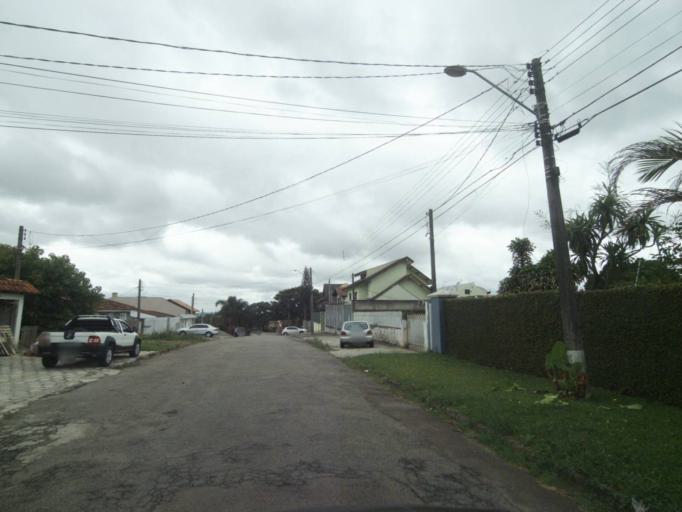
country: BR
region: Parana
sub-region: Curitiba
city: Curitiba
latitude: -25.4672
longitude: -49.3302
